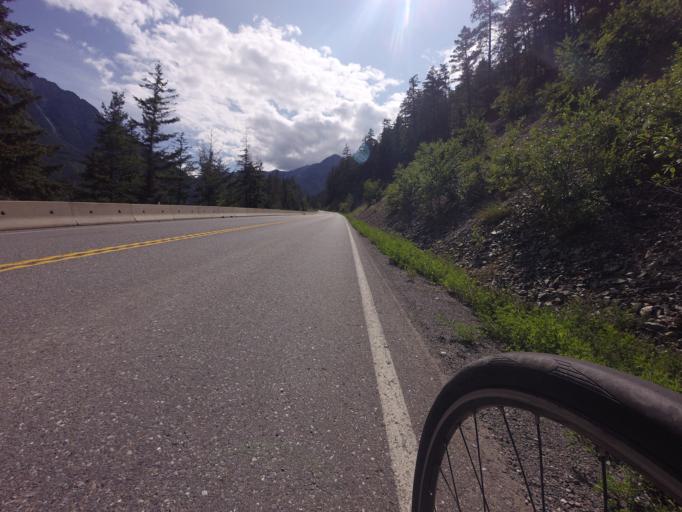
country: CA
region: British Columbia
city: Lillooet
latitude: 50.6522
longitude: -122.0151
